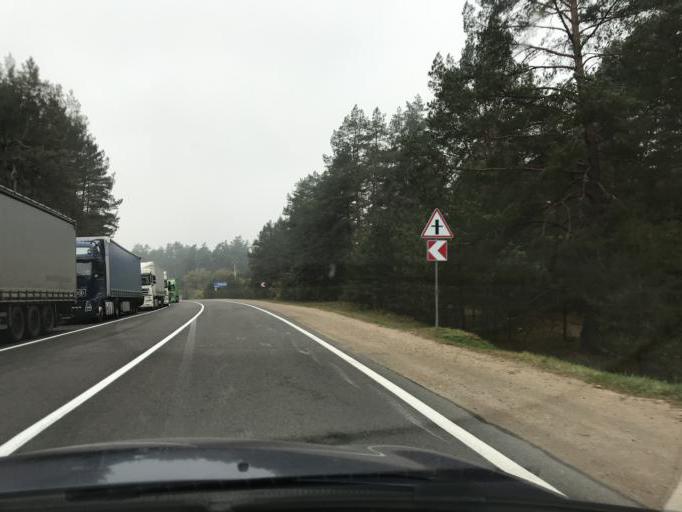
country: LT
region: Alytaus apskritis
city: Druskininkai
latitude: 53.9315
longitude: 23.9407
